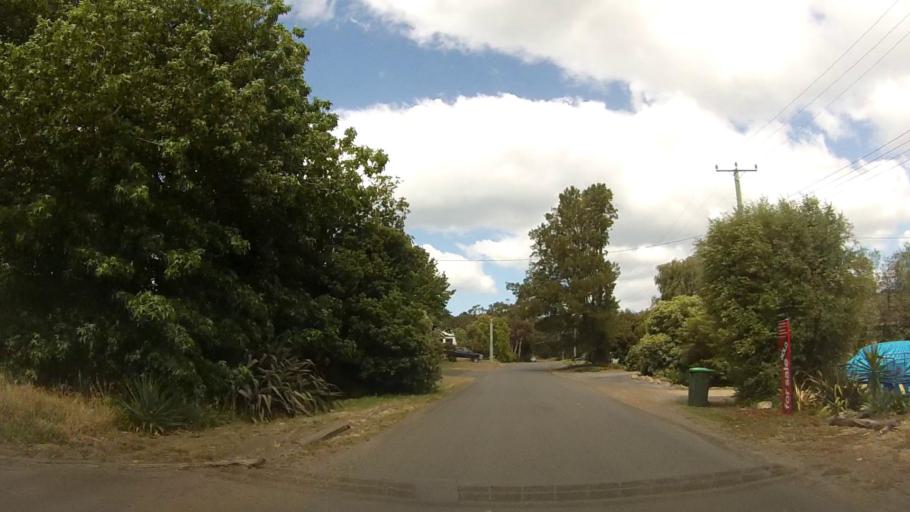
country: AU
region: Tasmania
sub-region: Clarence
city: Seven Mile Beach
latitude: -42.8558
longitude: 147.5078
